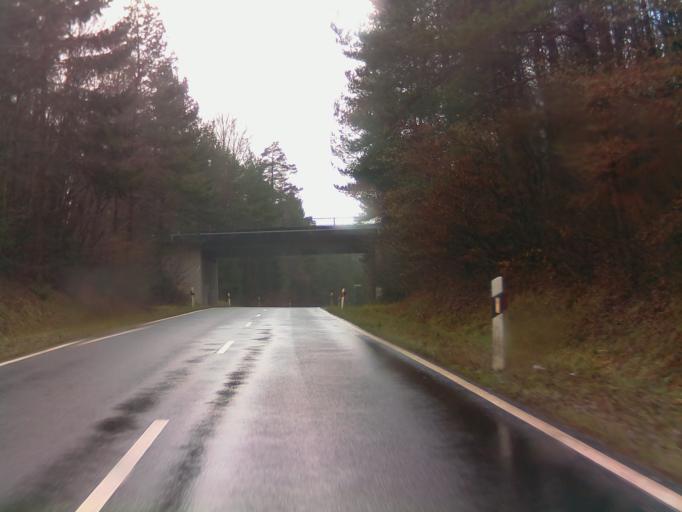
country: DE
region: Hesse
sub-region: Regierungsbezirk Kassel
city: Neuhof
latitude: 50.4623
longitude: 9.6579
